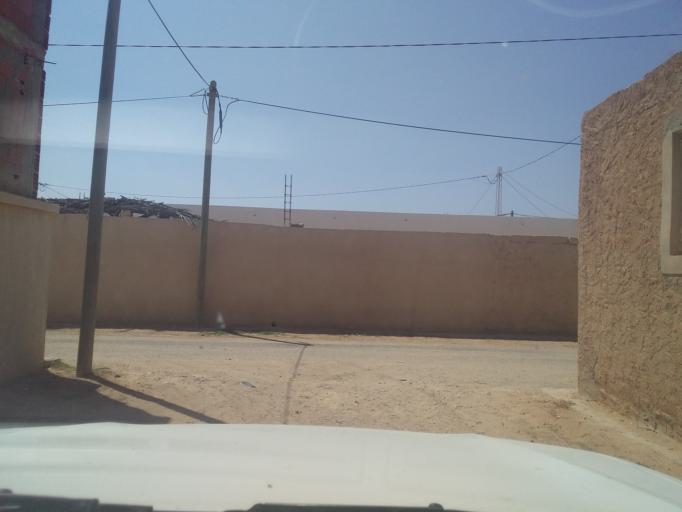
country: TN
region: Qabis
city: Matmata
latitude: 33.5912
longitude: 10.2833
